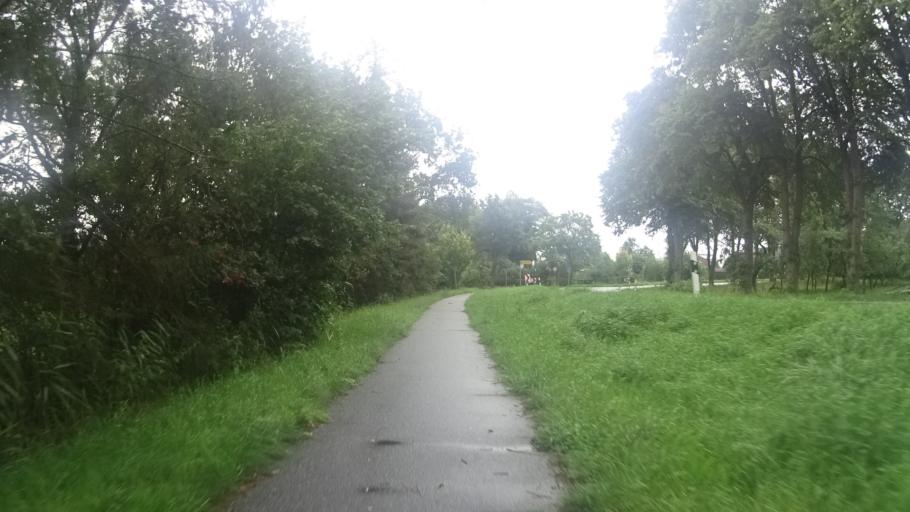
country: DE
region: Schleswig-Holstein
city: Seeth-Ekholt
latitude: 53.7569
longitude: 9.7303
